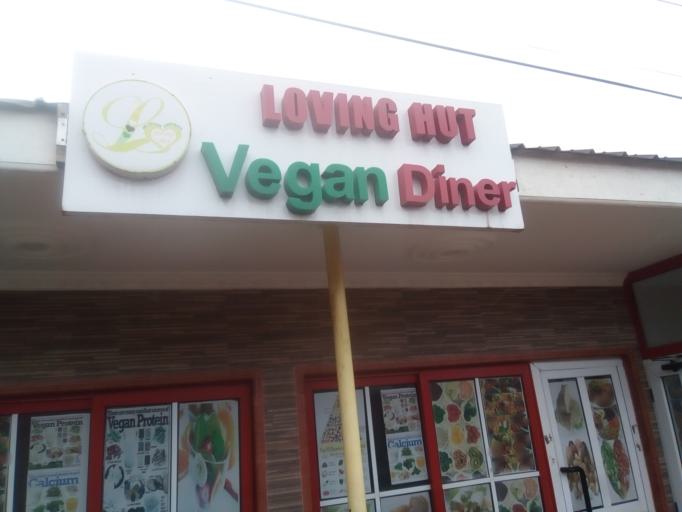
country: GH
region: Greater Accra
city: Dome
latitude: 5.6070
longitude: -0.2558
